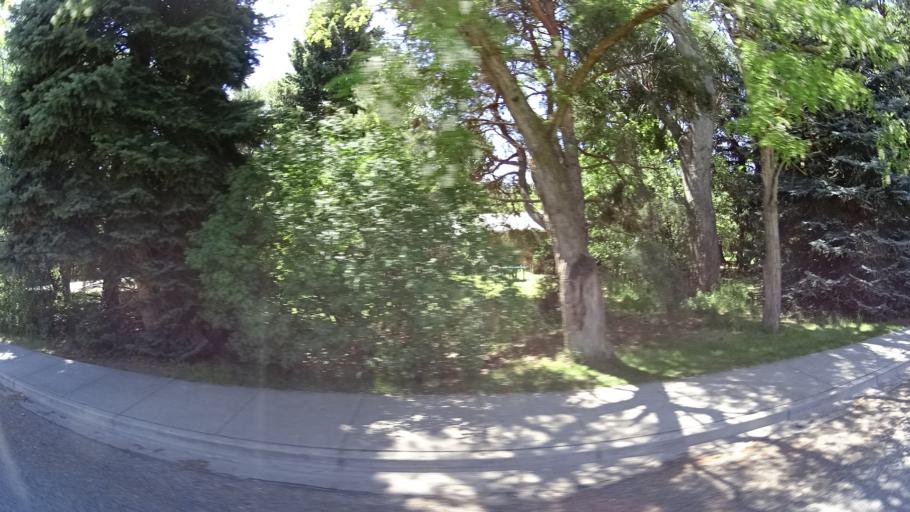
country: US
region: Idaho
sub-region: Ada County
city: Boise
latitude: 43.5677
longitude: -116.1551
